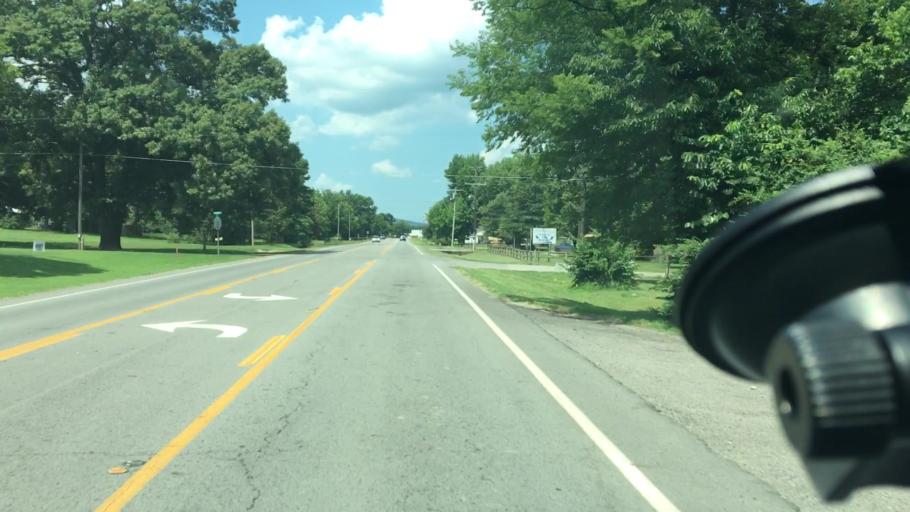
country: US
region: Arkansas
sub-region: Logan County
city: Paris
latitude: 35.2928
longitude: -93.7027
